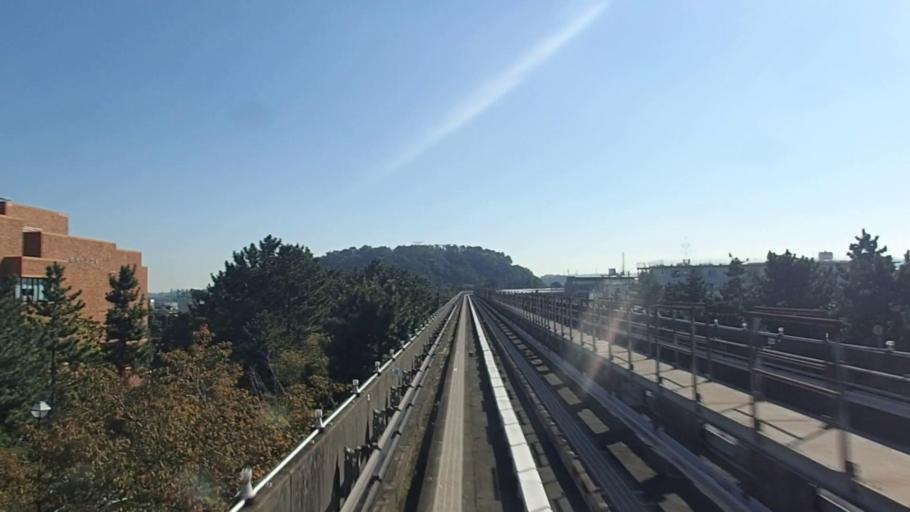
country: JP
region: Kanagawa
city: Yokosuka
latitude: 35.3347
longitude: 139.6326
